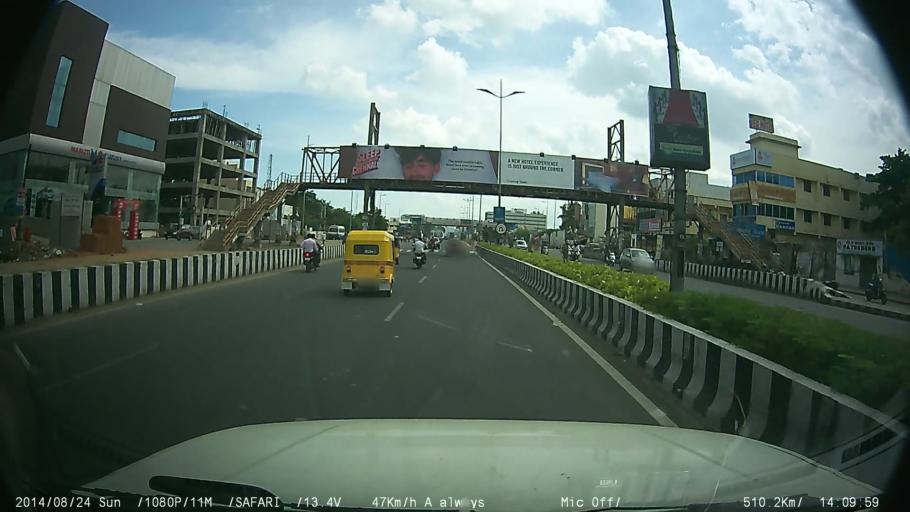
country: IN
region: Tamil Nadu
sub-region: Kancheepuram
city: Perungudi
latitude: 12.9591
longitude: 80.2446
